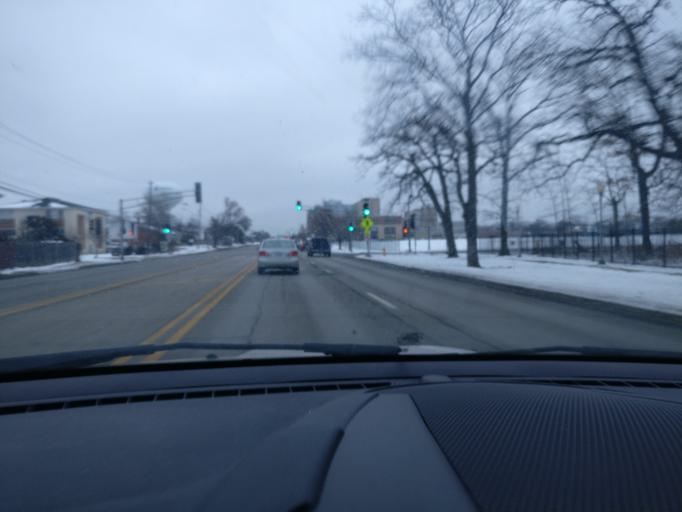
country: US
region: Illinois
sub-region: Cook County
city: Des Plaines
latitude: 42.0395
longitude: -87.8560
